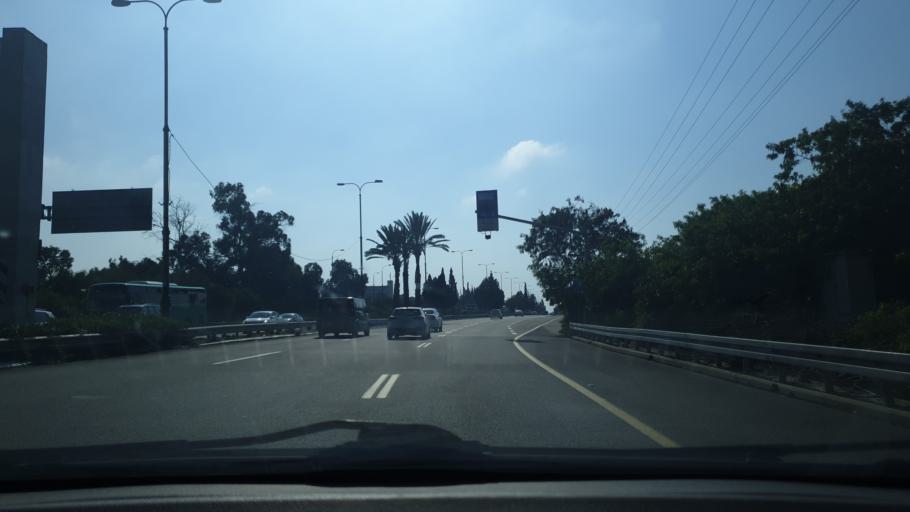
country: IL
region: Central District
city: Bet Dagan
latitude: 31.9977
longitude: 34.8183
